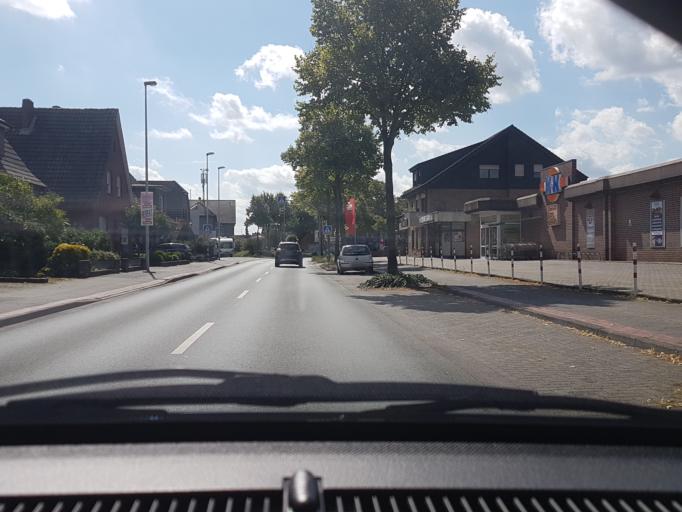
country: DE
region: North Rhine-Westphalia
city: Emsdetten
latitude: 52.1631
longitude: 7.5269
